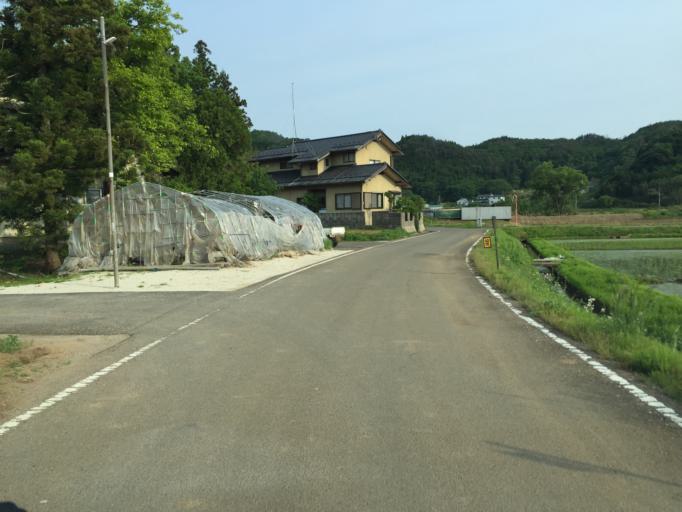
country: JP
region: Fukushima
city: Fukushima-shi
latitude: 37.7075
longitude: 140.4338
